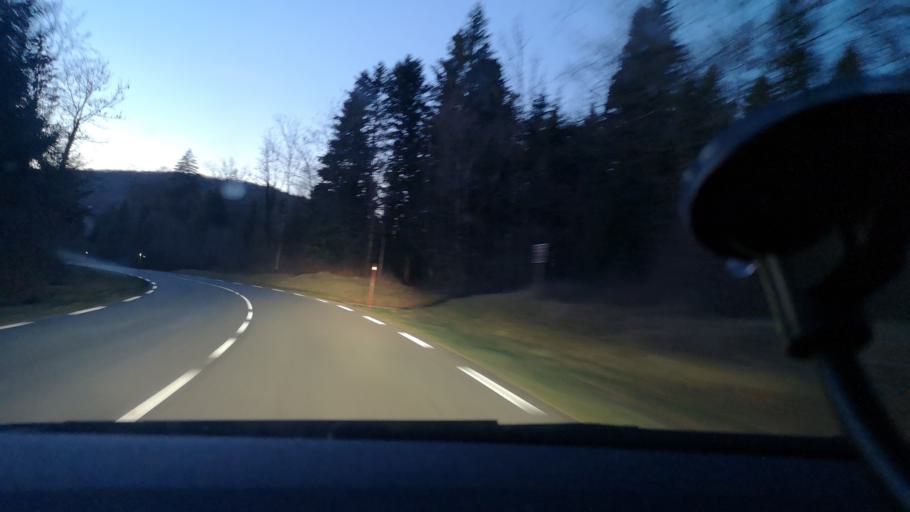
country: FR
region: Franche-Comte
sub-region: Departement du Jura
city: Champagnole
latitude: 46.7568
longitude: 5.9511
